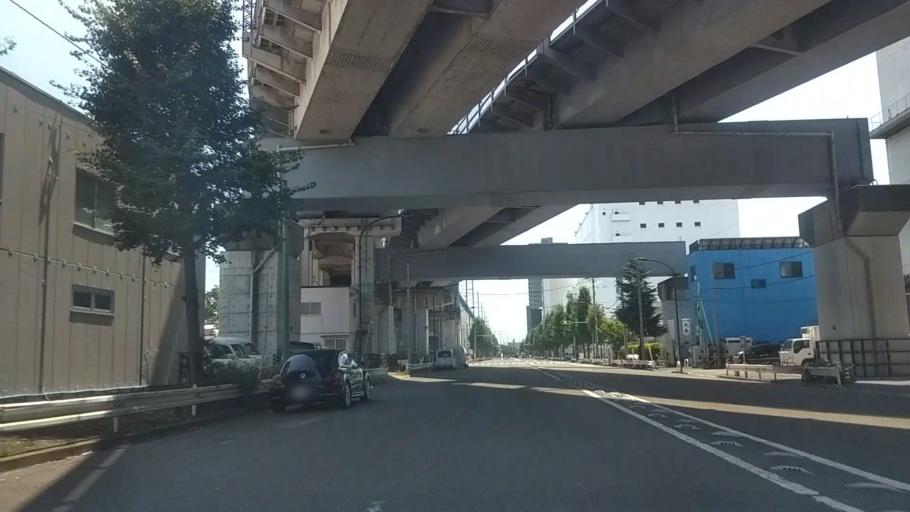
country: JP
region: Tokyo
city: Tokyo
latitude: 35.6290
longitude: 139.7546
